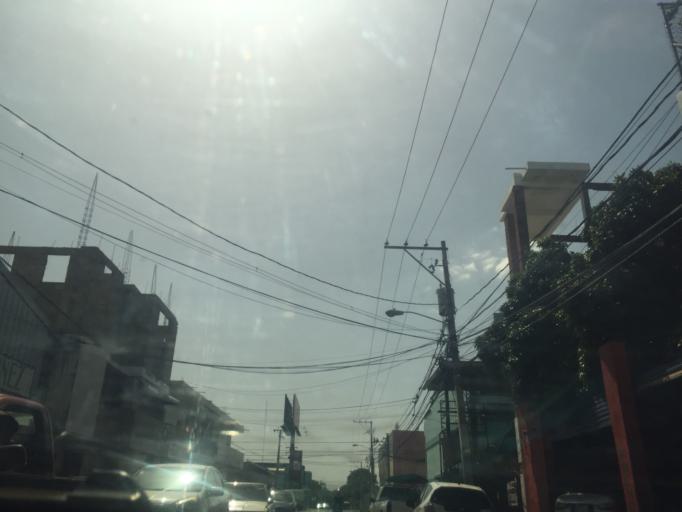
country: DO
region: Santiago
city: Santiago de los Caballeros
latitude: 19.4585
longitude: -70.6988
